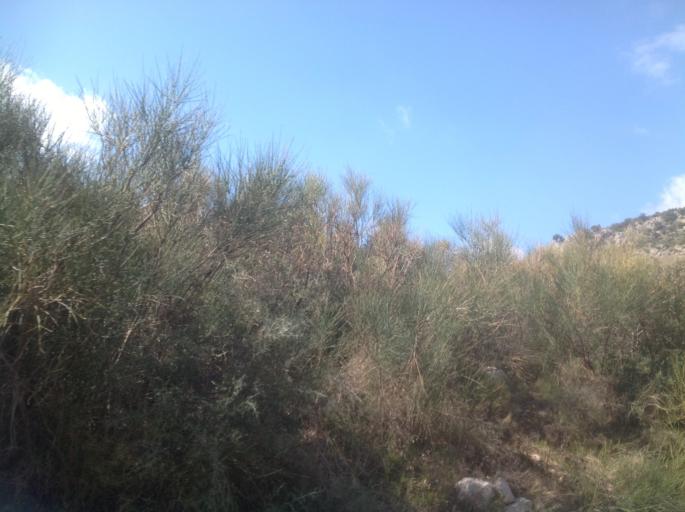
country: IT
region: Calabria
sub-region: Provincia di Cosenza
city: Civita
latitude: 39.8259
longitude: 16.3089
